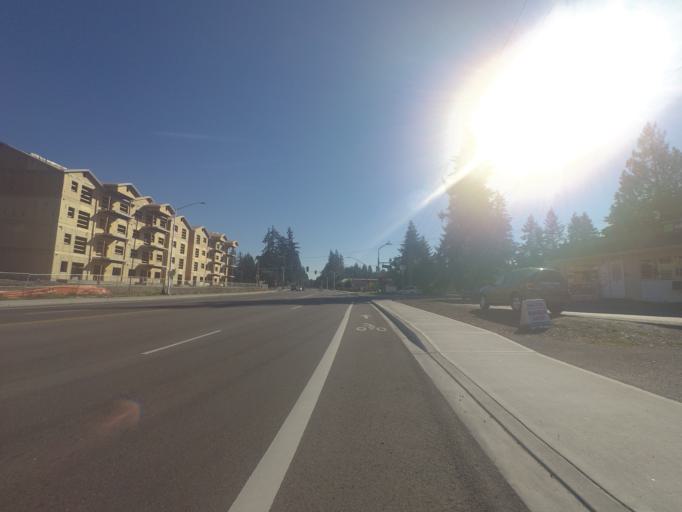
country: US
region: Washington
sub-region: Pierce County
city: McChord Air Force Base
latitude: 47.1431
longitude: -122.5045
